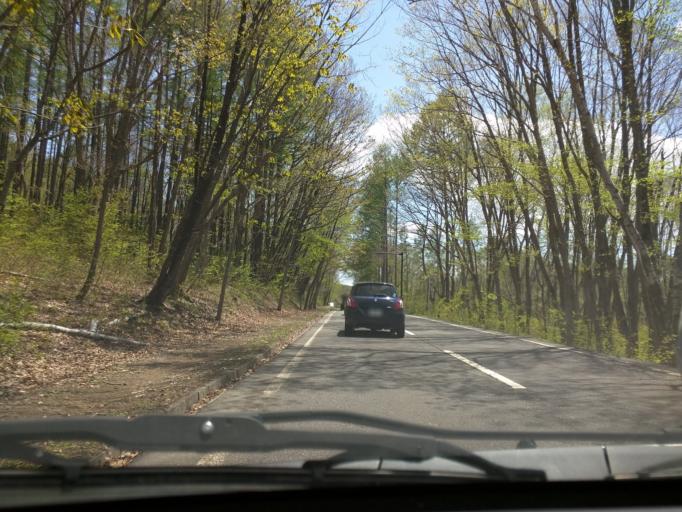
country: JP
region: Nagano
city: Nagano-shi
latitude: 36.7203
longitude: 138.0965
